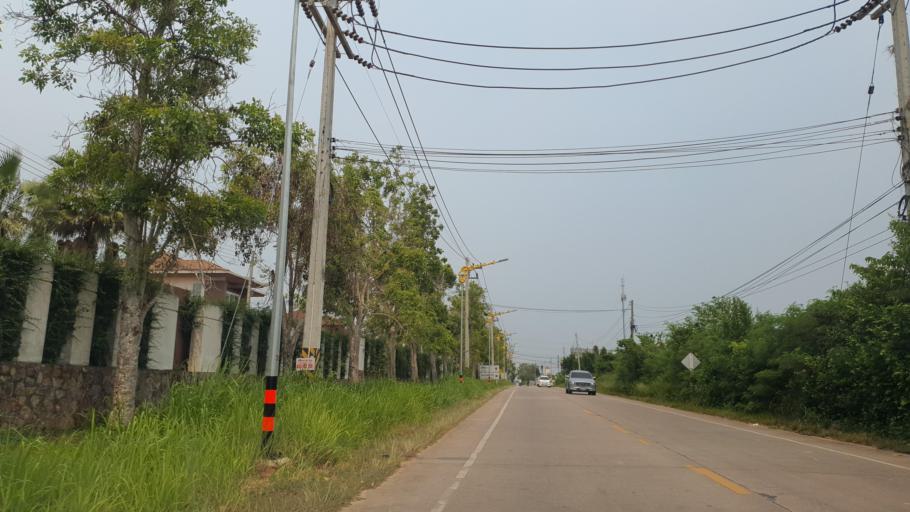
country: TH
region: Chon Buri
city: Phatthaya
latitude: 12.8950
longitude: 100.9222
